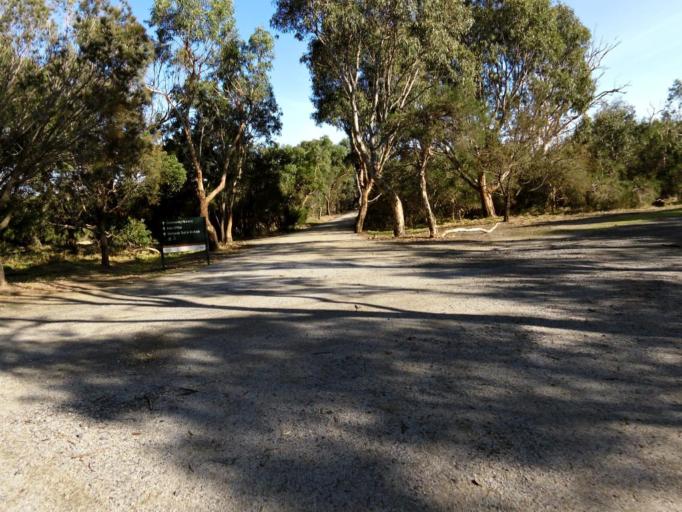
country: AU
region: Victoria
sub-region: Kingston
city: Waterways
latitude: -38.0078
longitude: 145.1322
